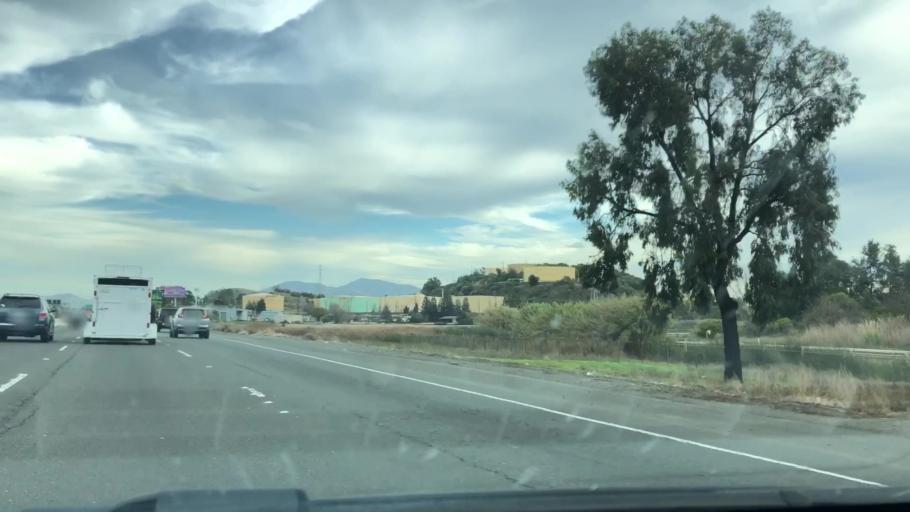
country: US
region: California
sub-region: Contra Costa County
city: Vine Hill
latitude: 38.0233
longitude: -122.1050
